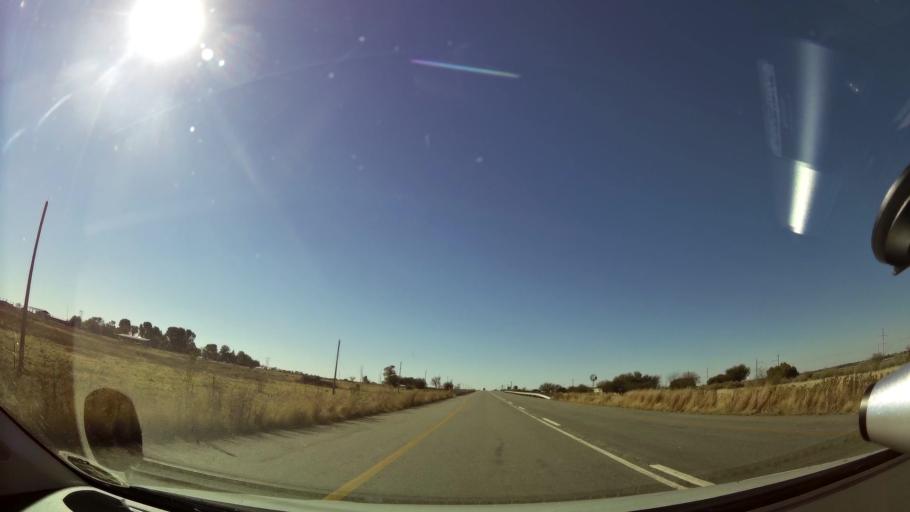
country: ZA
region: North-West
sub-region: Dr Ruth Segomotsi Mompati District Municipality
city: Bloemhof
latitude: -27.6797
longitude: 25.4639
